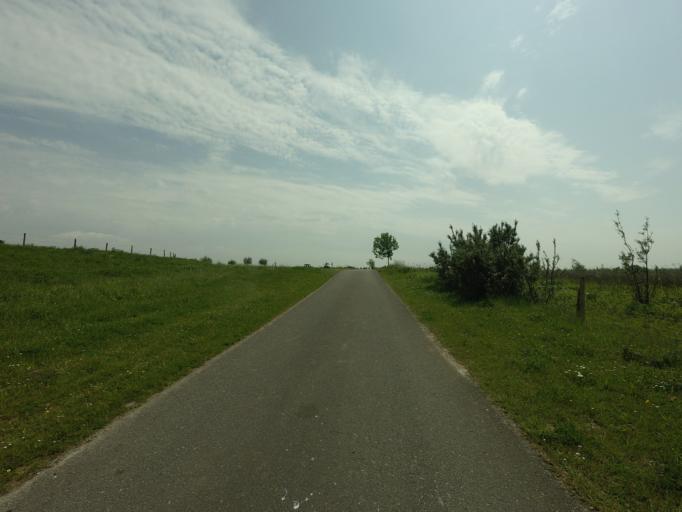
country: NL
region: North Brabant
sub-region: Gemeente Steenbergen
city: Dinteloord
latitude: 51.7365
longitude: 4.3432
